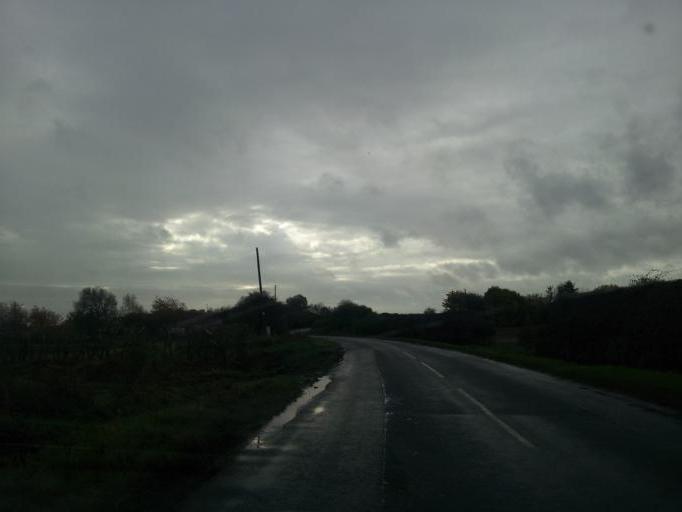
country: GB
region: England
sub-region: Lincolnshire
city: Long Bennington
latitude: 53.0146
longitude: -0.8043
